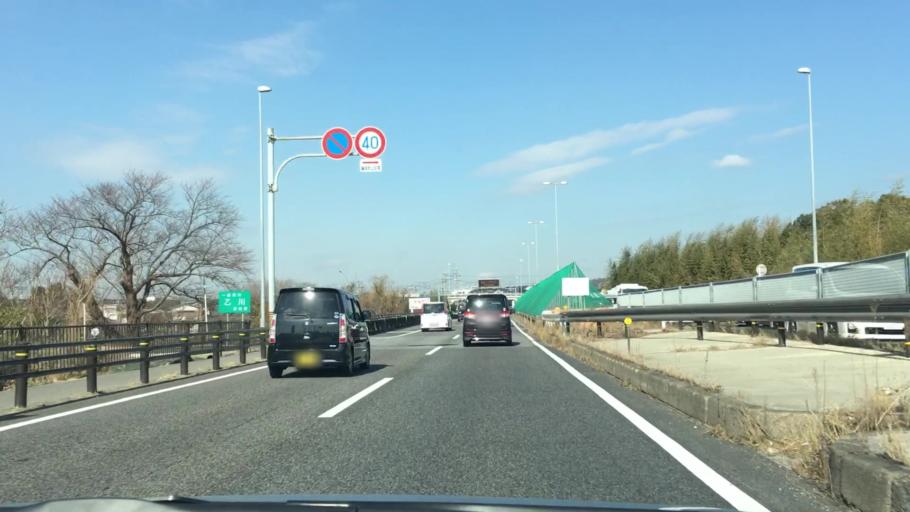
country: JP
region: Aichi
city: Okazaki
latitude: 34.9330
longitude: 137.1965
